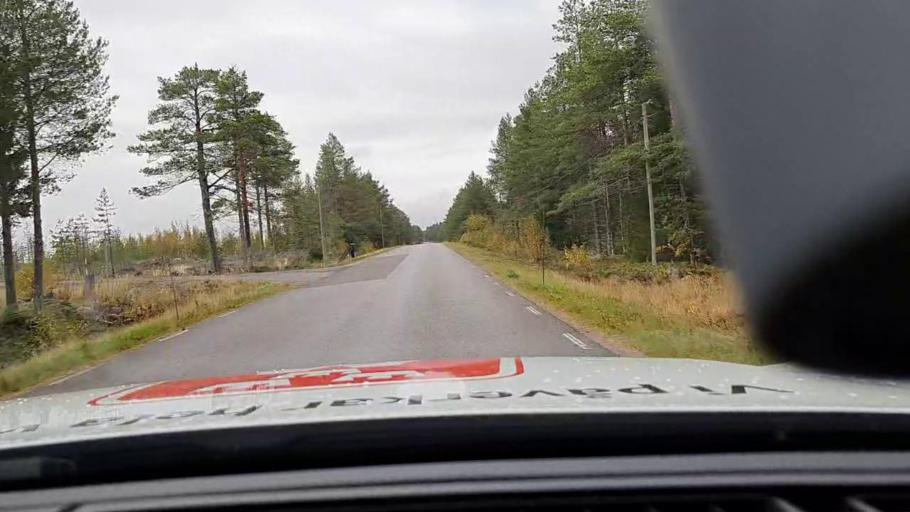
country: SE
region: Norrbotten
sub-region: Haparanda Kommun
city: Haparanda
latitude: 65.7788
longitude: 23.9167
